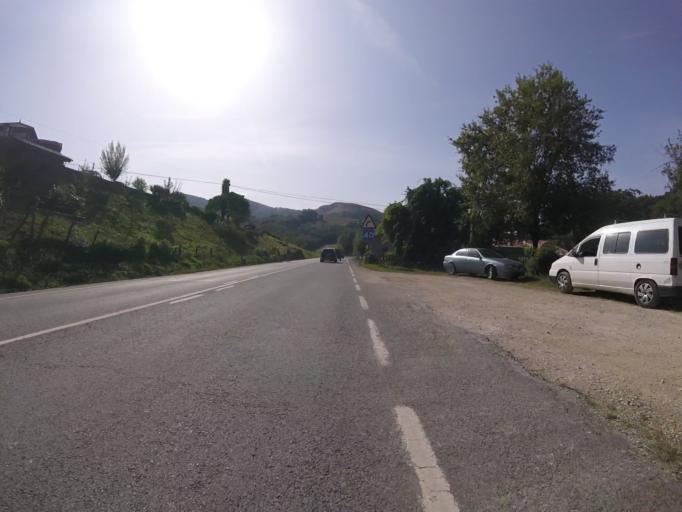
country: ES
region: Navarre
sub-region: Provincia de Navarra
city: Zugarramurdi
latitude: 43.1628
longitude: -1.4962
